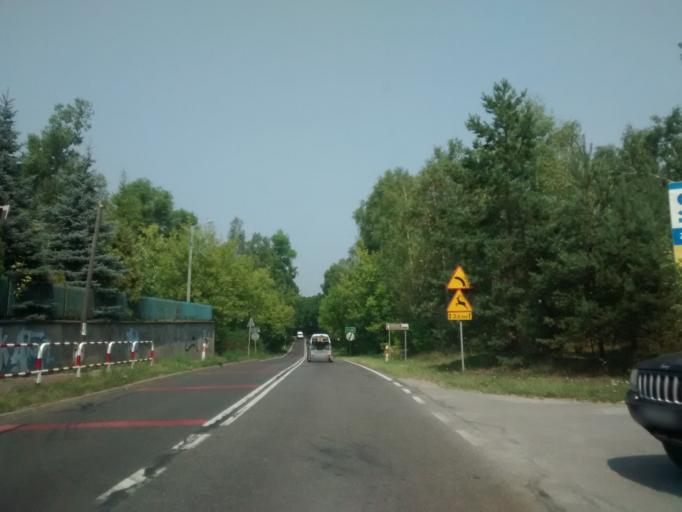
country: PL
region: Lesser Poland Voivodeship
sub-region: Powiat olkuski
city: Klucze
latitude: 50.3526
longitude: 19.5626
